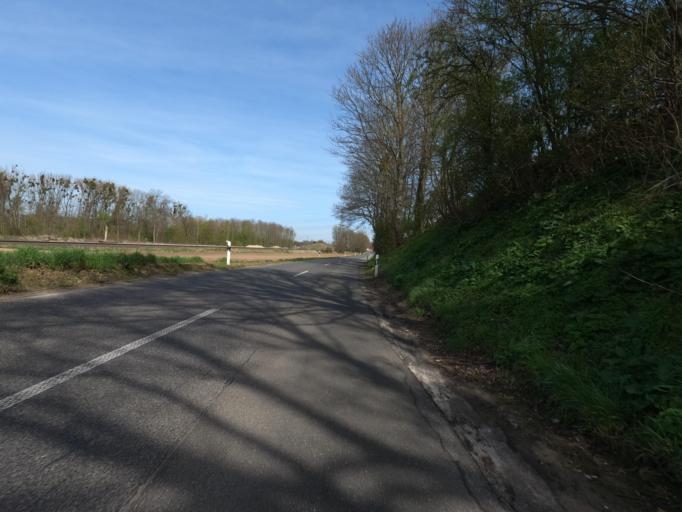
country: DE
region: North Rhine-Westphalia
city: Geilenkirchen
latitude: 50.9688
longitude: 6.1378
